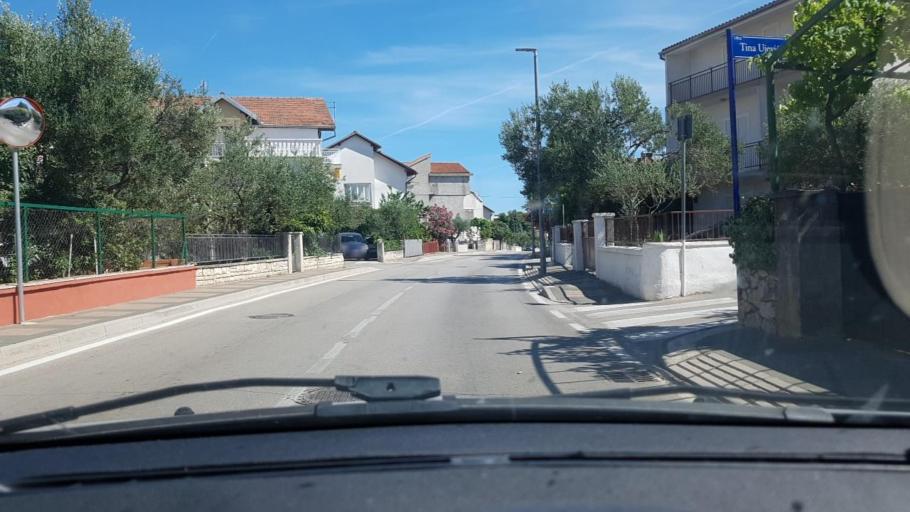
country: HR
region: Sibensko-Kniniska
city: Vodice
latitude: 43.7585
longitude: 15.7889
